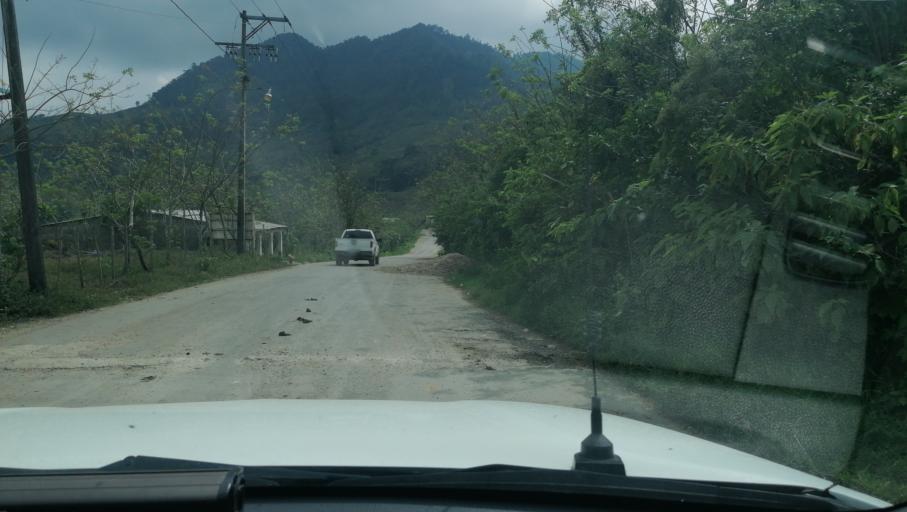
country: MX
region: Chiapas
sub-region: Francisco Leon
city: San Miguel la Sardina
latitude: 17.2838
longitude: -93.2744
